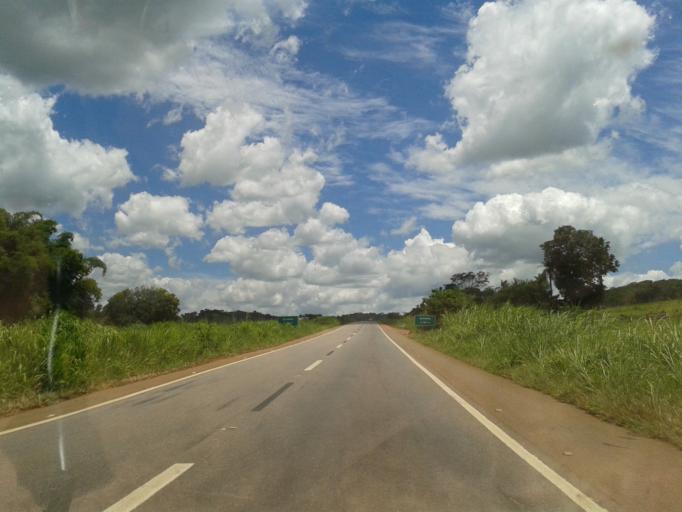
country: BR
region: Goias
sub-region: Neropolis
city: Neropolis
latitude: -16.2874
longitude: -49.2846
